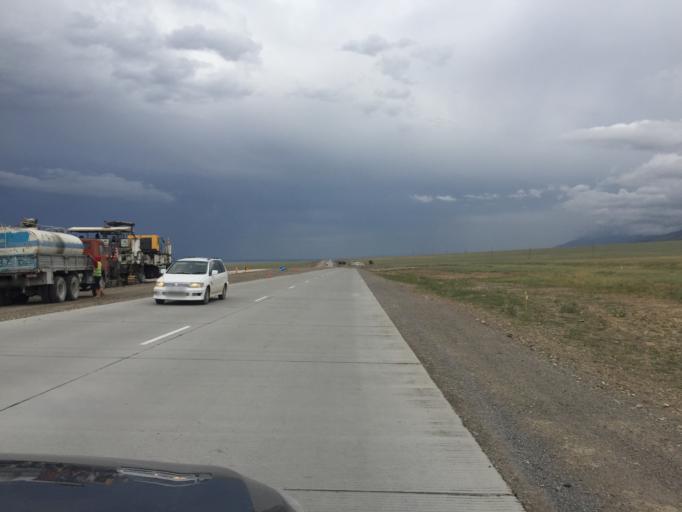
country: KG
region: Chuy
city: Ivanovka
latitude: 43.3862
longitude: 75.1559
